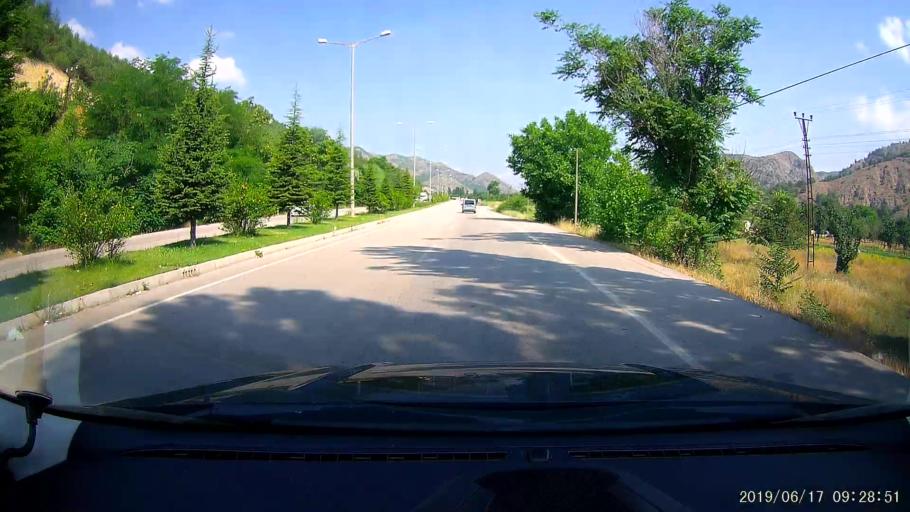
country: TR
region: Amasya
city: Amasya
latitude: 40.6927
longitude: 35.8195
